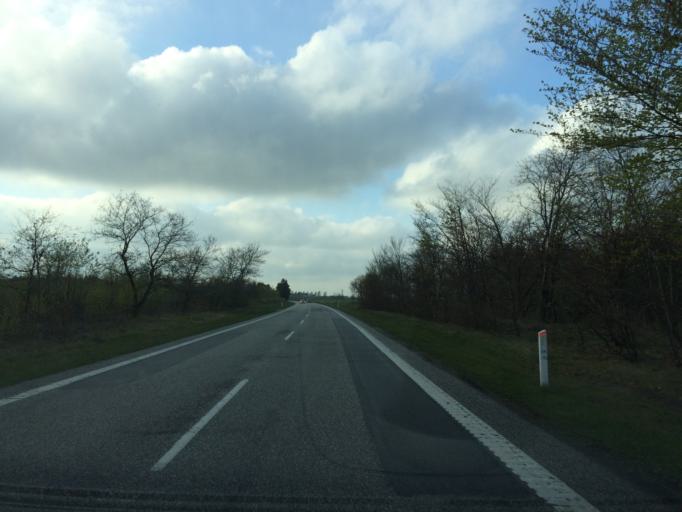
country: DK
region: Central Jutland
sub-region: Viborg Kommune
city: Karup
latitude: 56.3240
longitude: 9.1112
